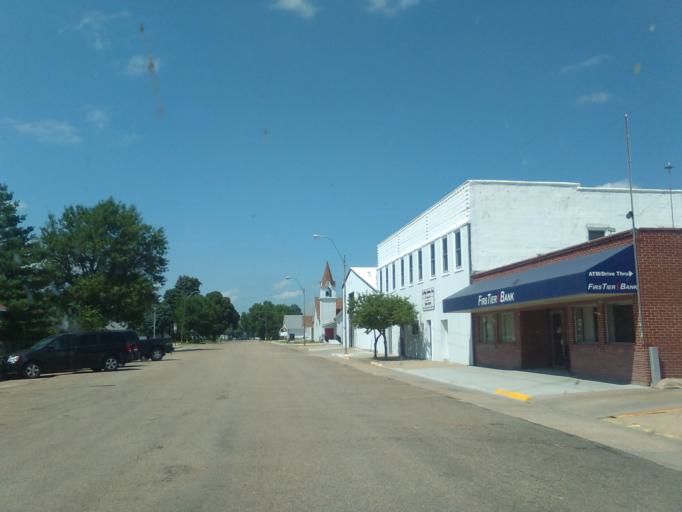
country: US
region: Nebraska
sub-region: Phelps County
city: Holdrege
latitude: 40.7184
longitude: -99.3732
